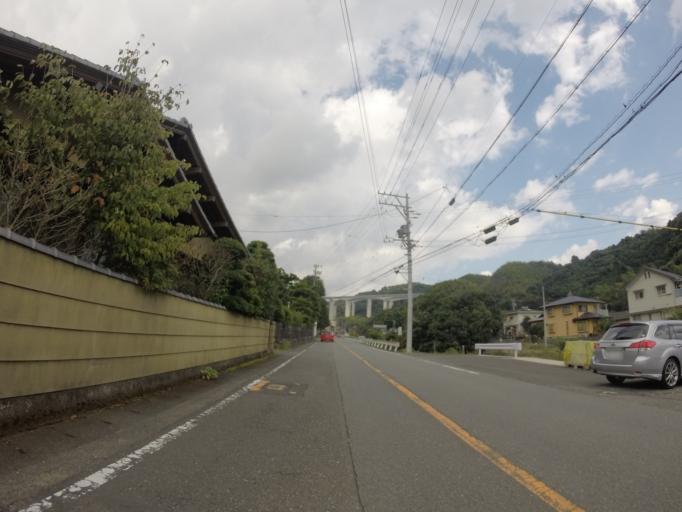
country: JP
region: Shizuoka
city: Shizuoka-shi
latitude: 35.0667
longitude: 138.4693
